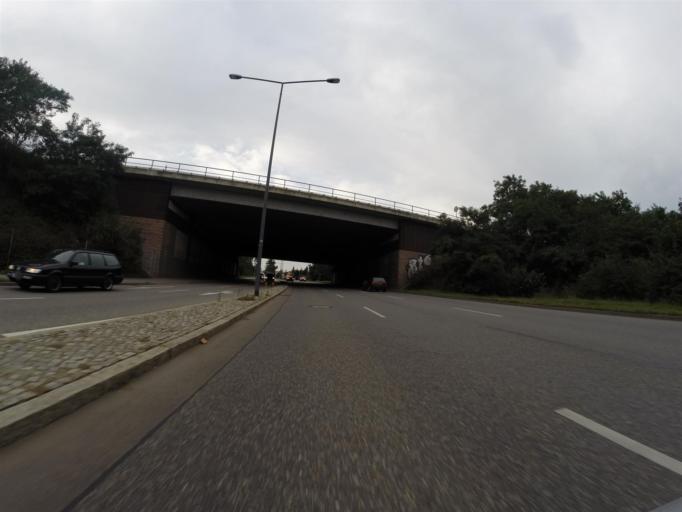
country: DE
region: Saxony
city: Albertstadt
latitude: 51.1067
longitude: 13.7348
